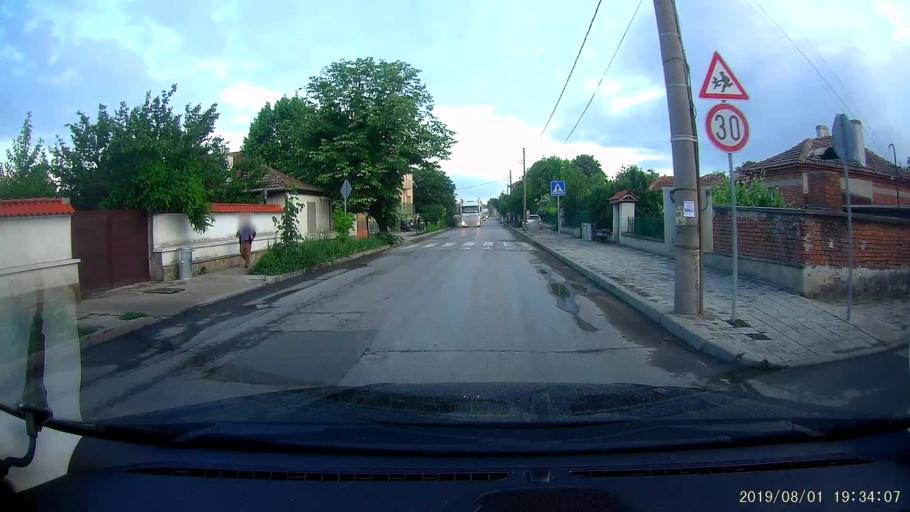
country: BG
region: Burgas
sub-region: Obshtina Sungurlare
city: Sungurlare
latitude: 42.7729
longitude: 26.8784
